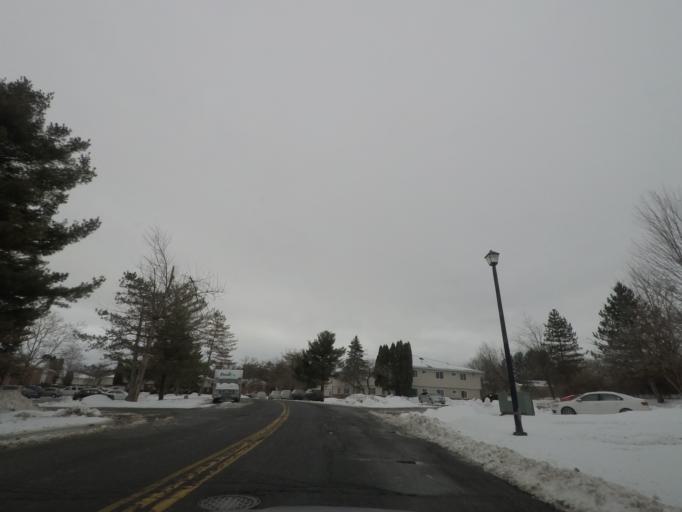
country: US
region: New York
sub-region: Albany County
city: Watervliet
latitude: 42.7299
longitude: -73.7302
